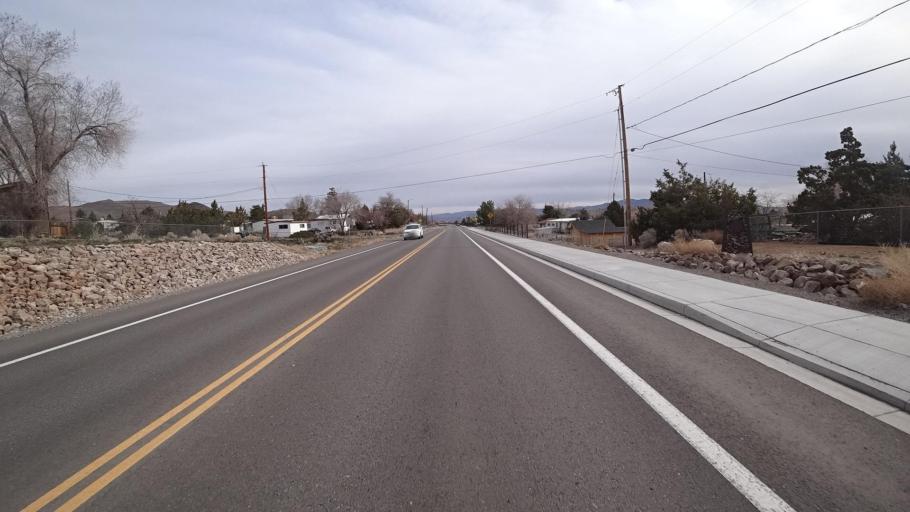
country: US
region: Nevada
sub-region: Washoe County
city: Sun Valley
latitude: 39.6126
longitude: -119.7737
